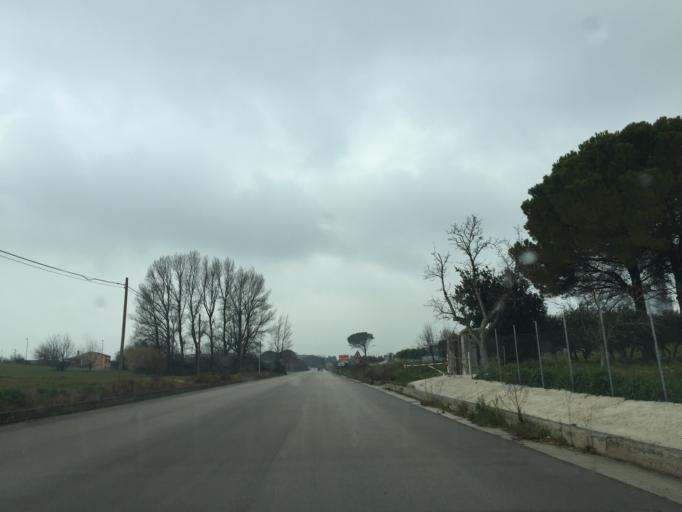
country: IT
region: Apulia
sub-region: Provincia di Foggia
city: Troia
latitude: 41.3730
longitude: 15.3492
